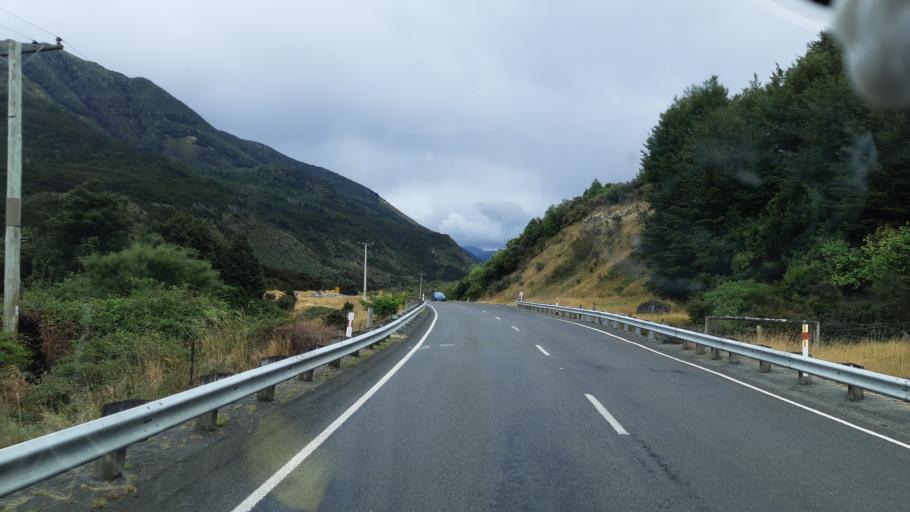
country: NZ
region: Canterbury
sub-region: Hurunui District
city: Amberley
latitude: -42.5711
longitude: 172.3661
